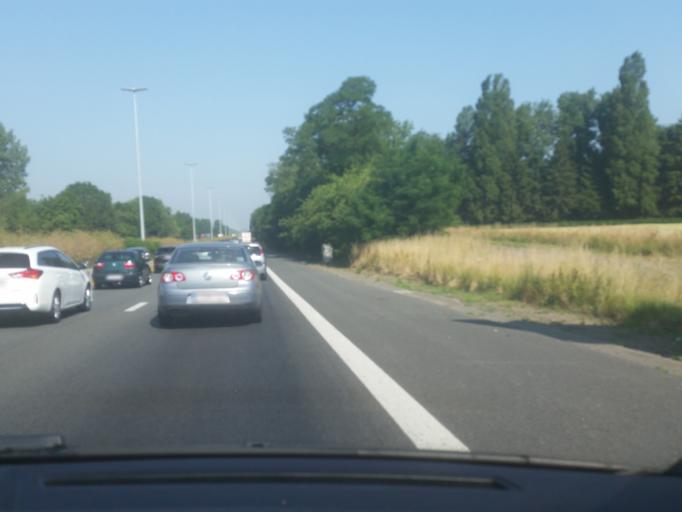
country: BE
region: Flanders
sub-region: Provincie Oost-Vlaanderen
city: Sint-Lievens-Houtem
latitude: 50.9448
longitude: 3.9048
